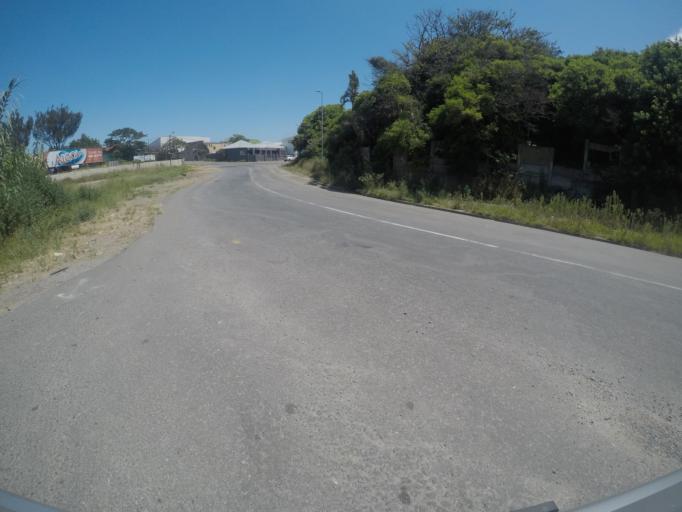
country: ZA
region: Eastern Cape
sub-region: Buffalo City Metropolitan Municipality
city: East London
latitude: -33.0117
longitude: 27.9152
